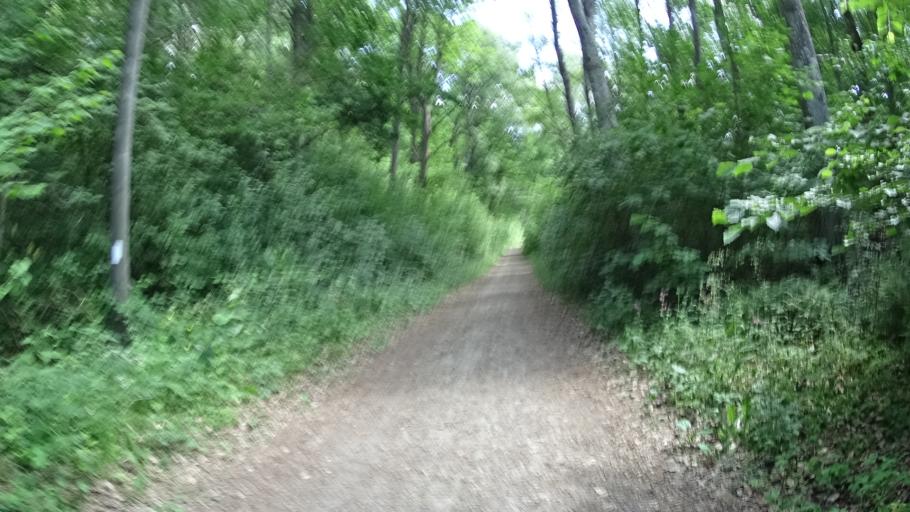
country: FI
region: Uusimaa
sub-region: Raaseporin
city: Pohja
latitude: 60.1111
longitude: 23.5469
